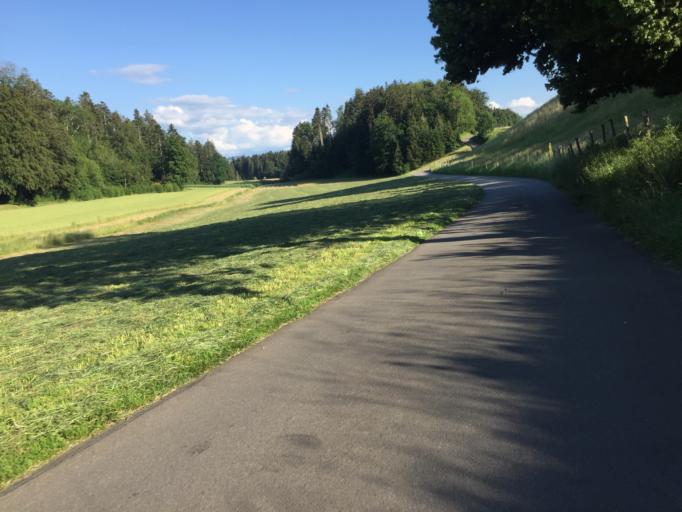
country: CH
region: Bern
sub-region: Bern-Mittelland District
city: Niederwichtrach
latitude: 46.8394
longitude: 7.5820
